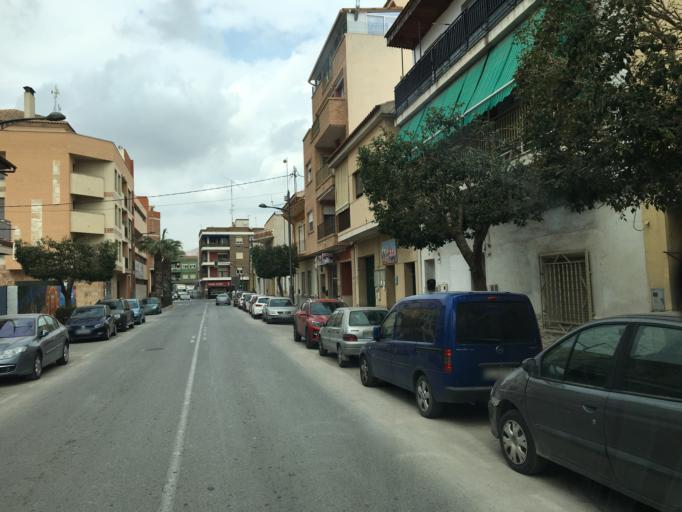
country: ES
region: Murcia
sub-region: Murcia
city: Beniel
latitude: 38.0451
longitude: -1.0012
